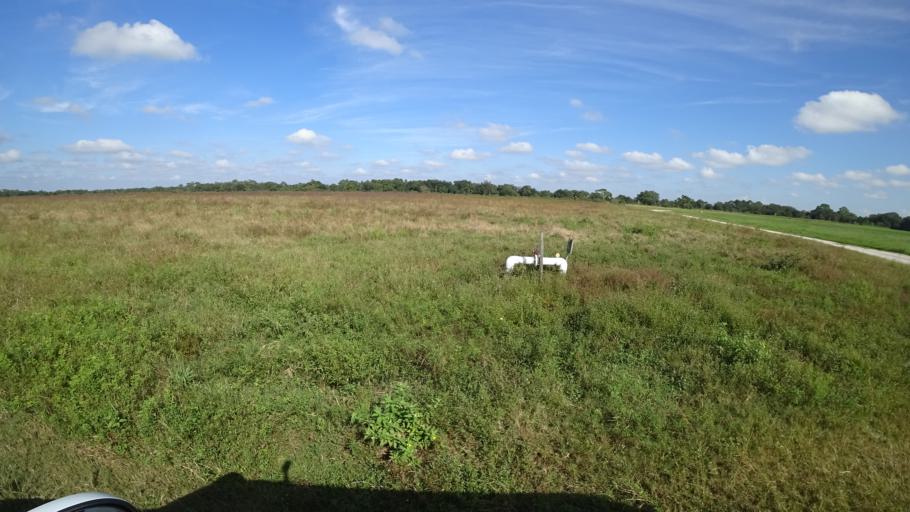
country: US
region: Florida
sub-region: Sarasota County
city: Lake Sarasota
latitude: 27.3634
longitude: -82.1574
